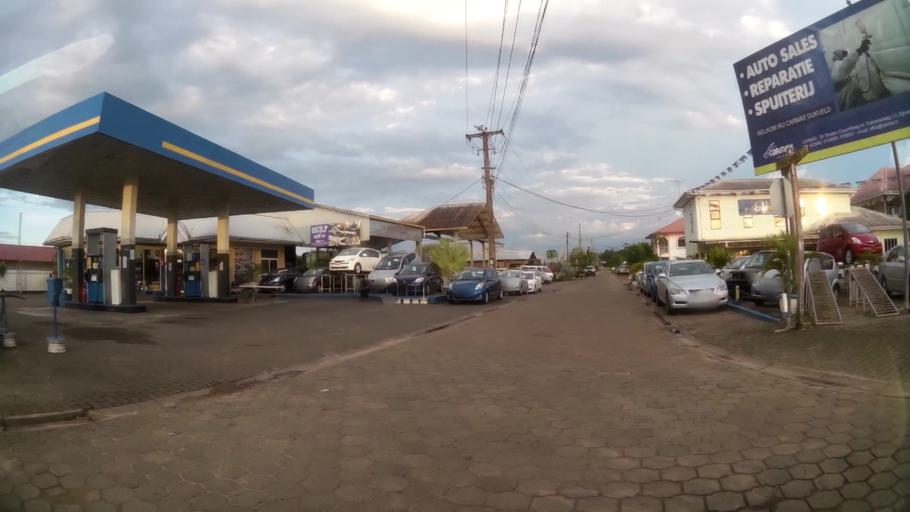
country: SR
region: Paramaribo
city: Paramaribo
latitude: 5.7791
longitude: -55.1677
